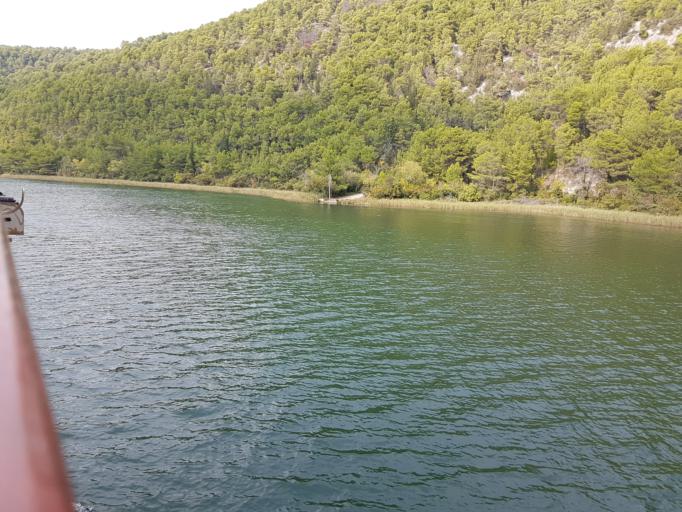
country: HR
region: Sibensko-Kniniska
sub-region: Grad Sibenik
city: Sibenik
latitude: 43.8191
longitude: 15.9484
